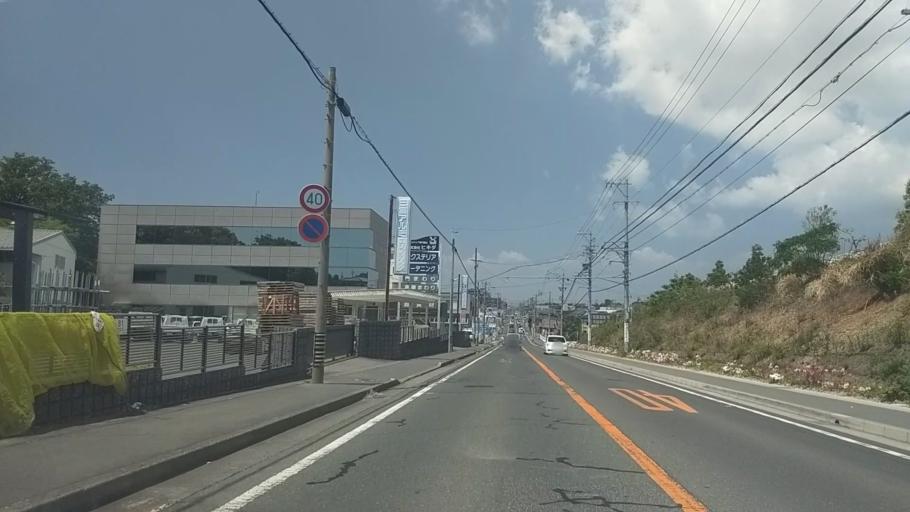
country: JP
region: Shizuoka
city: Hamamatsu
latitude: 34.7363
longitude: 137.7192
